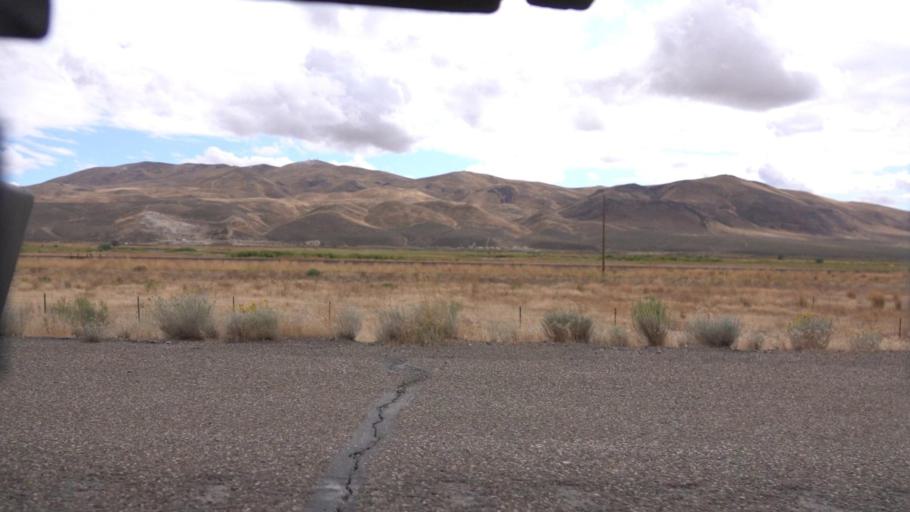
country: US
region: Nevada
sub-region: Elko County
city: Elko
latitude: 40.9193
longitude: -115.6869
